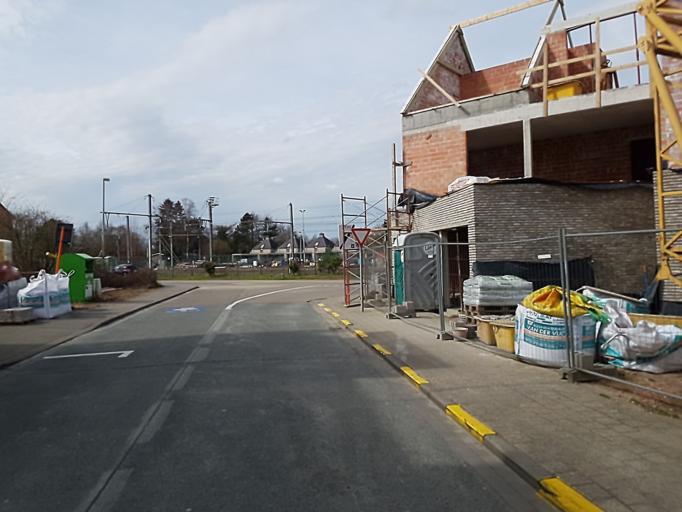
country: BE
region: Flanders
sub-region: Provincie Antwerpen
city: Mol
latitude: 51.1891
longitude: 5.1094
